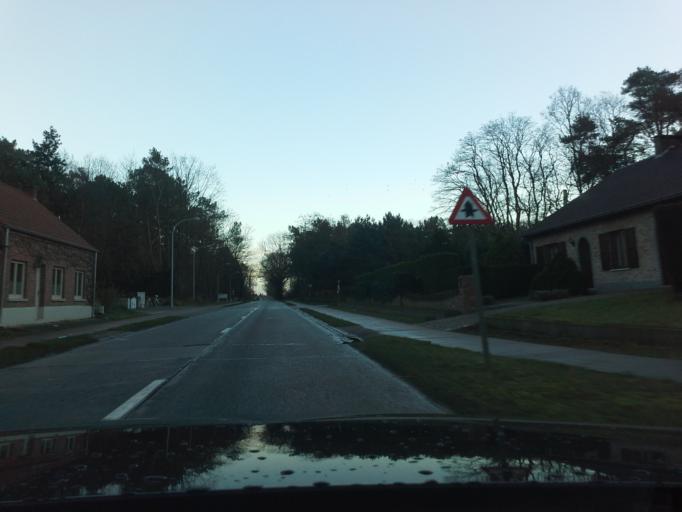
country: BE
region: Flanders
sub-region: Provincie Antwerpen
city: Meerhout
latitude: 51.1430
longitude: 5.0533
